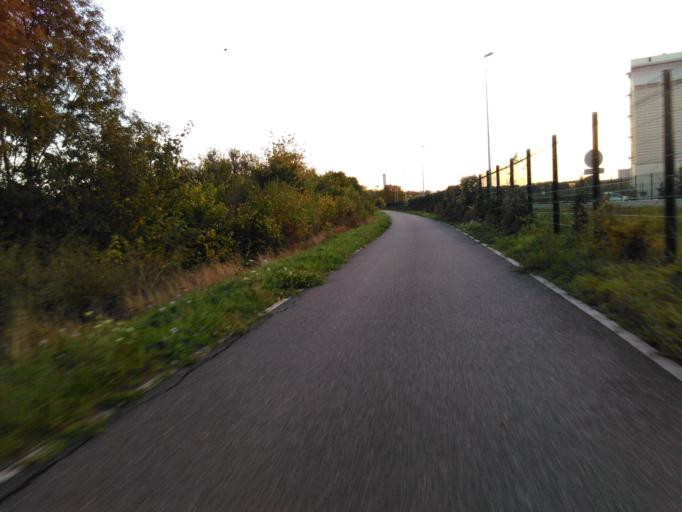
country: FR
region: Lorraine
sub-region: Departement de la Moselle
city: Saint-Julien-les-Metz
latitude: 49.1400
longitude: 6.1943
